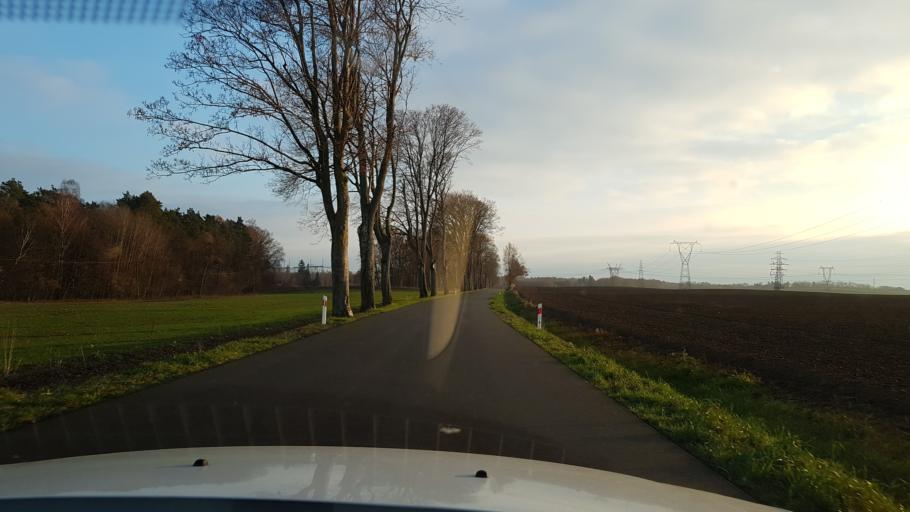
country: PL
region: West Pomeranian Voivodeship
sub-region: Koszalin
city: Koszalin
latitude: 54.1324
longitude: 16.0860
